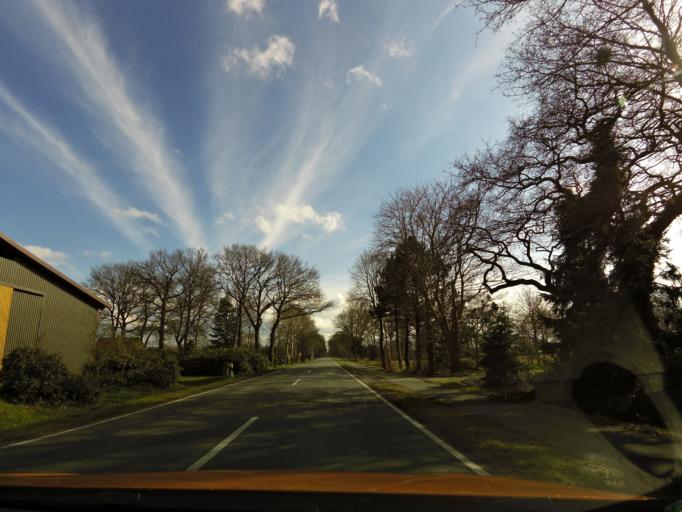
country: DE
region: Lower Saxony
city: Oldenburg
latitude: 53.0888
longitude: 8.2897
